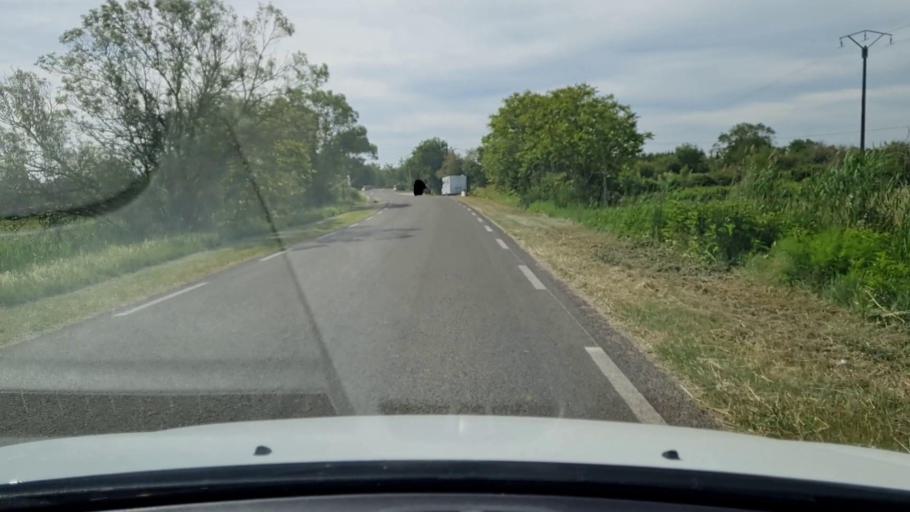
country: FR
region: Languedoc-Roussillon
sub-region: Departement du Gard
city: Aigues-Mortes
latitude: 43.6085
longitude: 4.2124
